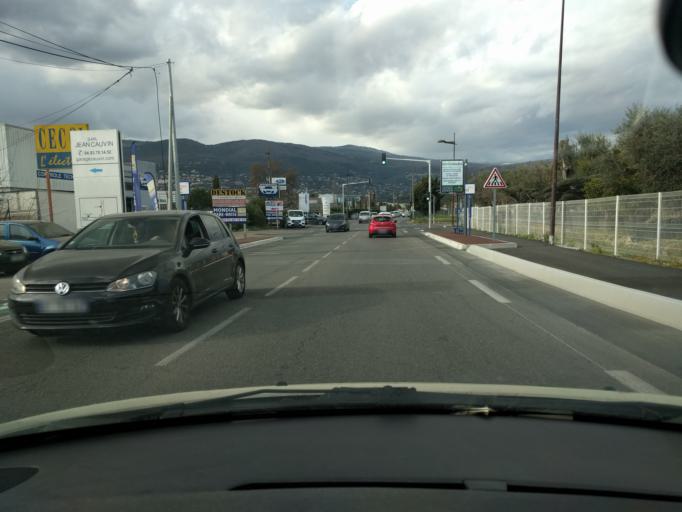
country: FR
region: Provence-Alpes-Cote d'Azur
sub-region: Departement des Alpes-Maritimes
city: Mouans-Sartoux
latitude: 43.6357
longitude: 6.9568
